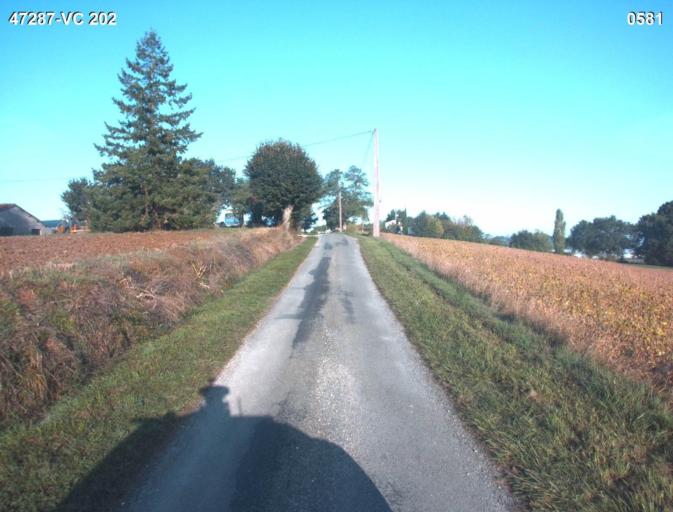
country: FR
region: Aquitaine
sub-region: Departement du Lot-et-Garonne
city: Laplume
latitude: 44.1152
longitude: 0.4642
